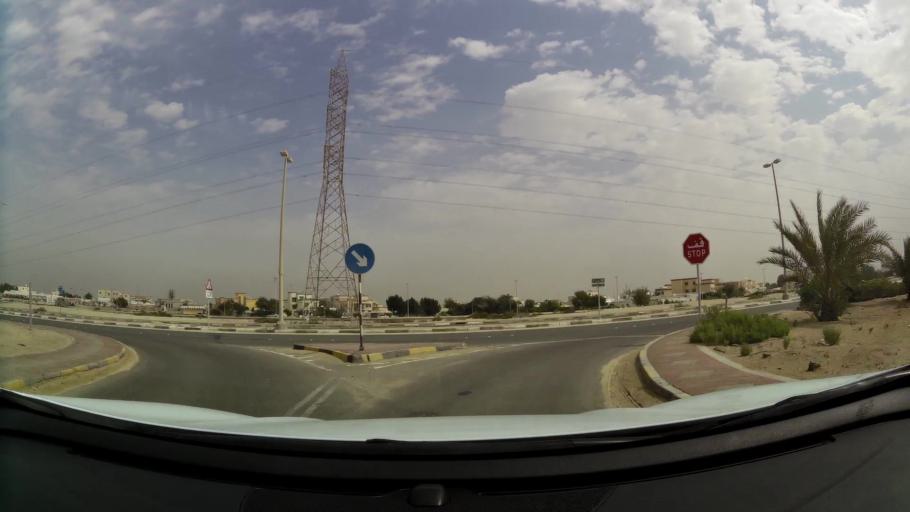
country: AE
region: Abu Dhabi
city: Abu Dhabi
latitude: 24.3140
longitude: 54.6366
